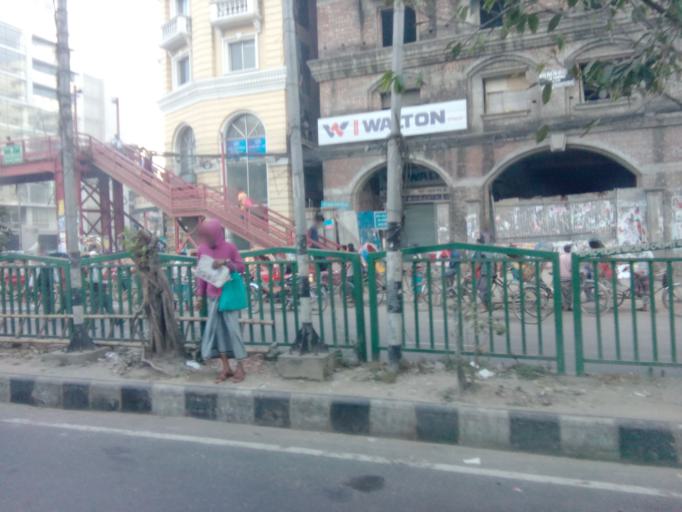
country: BD
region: Dhaka
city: Azimpur
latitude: 23.7463
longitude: 90.3952
